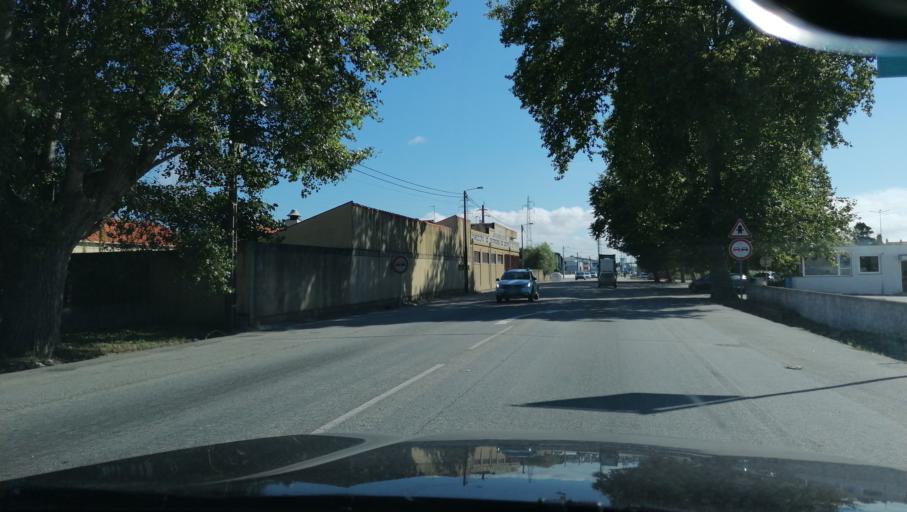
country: PT
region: Aveiro
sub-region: Aveiro
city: Aveiro
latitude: 40.6608
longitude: -8.6136
